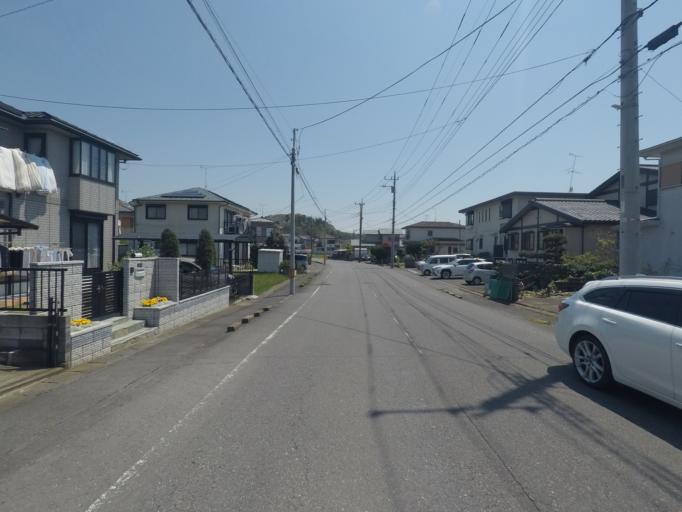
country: JP
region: Ibaraki
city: Ushiku
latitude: 35.9895
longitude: 140.1091
